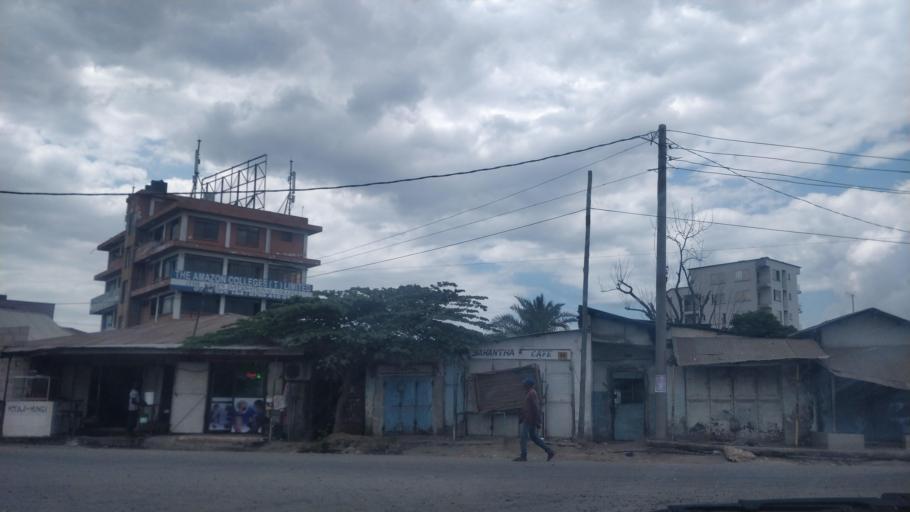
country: TZ
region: Dar es Salaam
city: Magomeni
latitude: -6.8039
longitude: 39.2456
